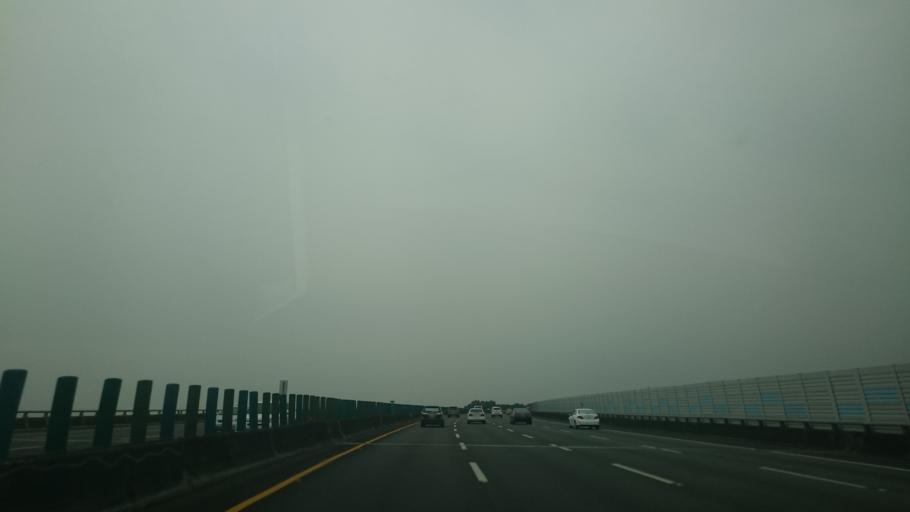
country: TW
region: Taiwan
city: Zhongxing New Village
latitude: 23.9694
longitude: 120.6486
